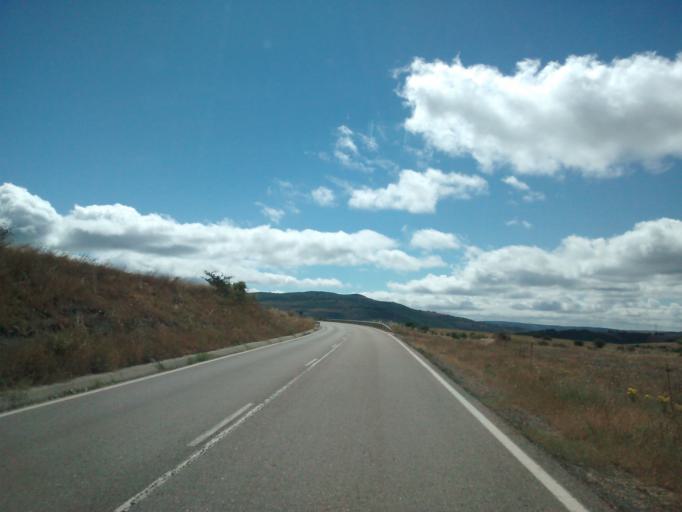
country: ES
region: Cantabria
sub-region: Provincia de Cantabria
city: Mataporquera
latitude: 42.9086
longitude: -4.1040
